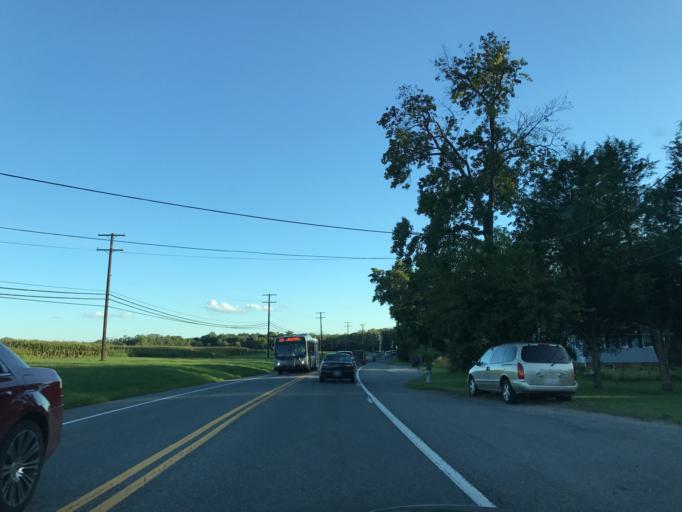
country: US
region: Maryland
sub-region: Prince George's County
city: Beltsville
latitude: 39.0271
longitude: -76.9012
